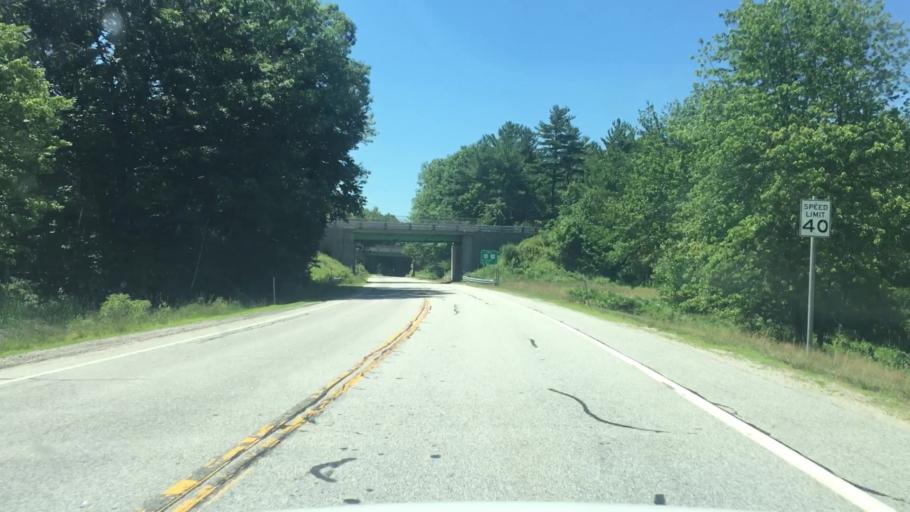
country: US
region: New Hampshire
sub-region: Merrimack County
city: Hopkinton
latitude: 43.1828
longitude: -71.6878
